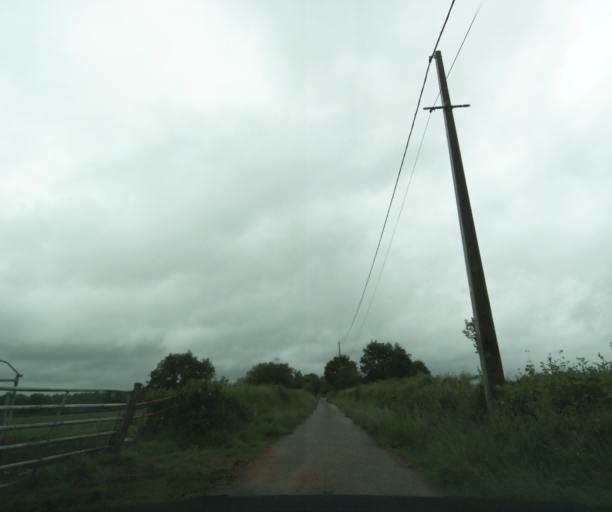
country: FR
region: Bourgogne
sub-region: Departement de Saone-et-Loire
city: Ciry-le-Noble
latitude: 46.5156
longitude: 4.3772
